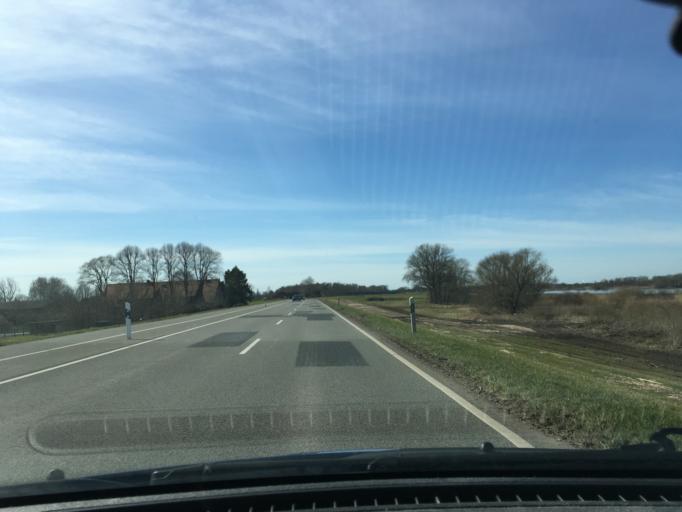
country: DE
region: Lower Saxony
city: Winsen
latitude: 53.3941
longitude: 10.2096
